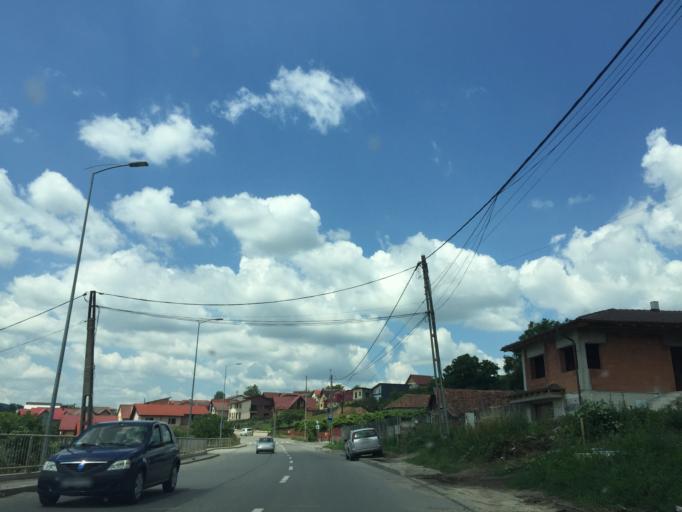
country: RO
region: Cluj
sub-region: Municipiul Cluj-Napoca
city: Cluj-Napoca
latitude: 46.8188
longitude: 23.5991
